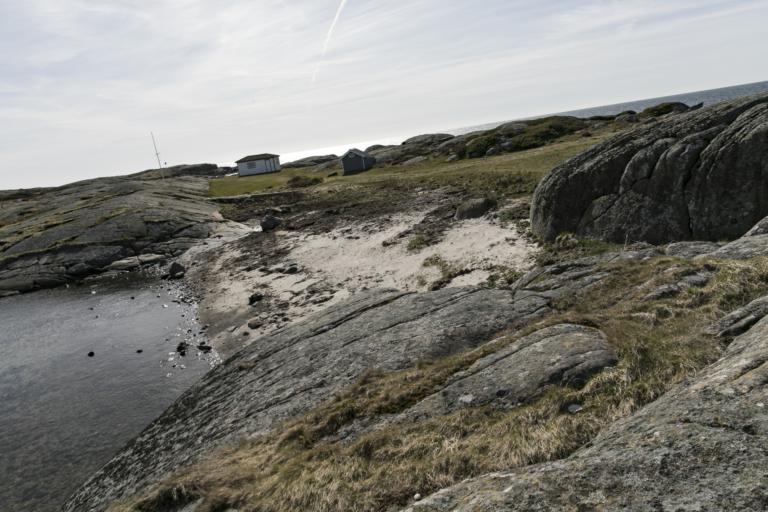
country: SE
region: Halland
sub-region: Varbergs Kommun
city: Varberg
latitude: 57.1124
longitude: 12.2145
